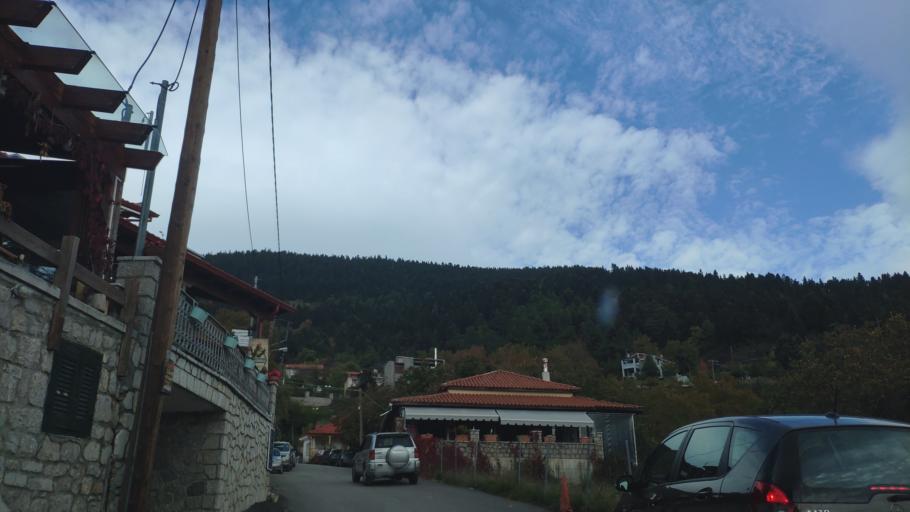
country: GR
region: Central Greece
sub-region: Nomos Fthiotidos
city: Stavros
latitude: 38.7401
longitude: 22.3376
